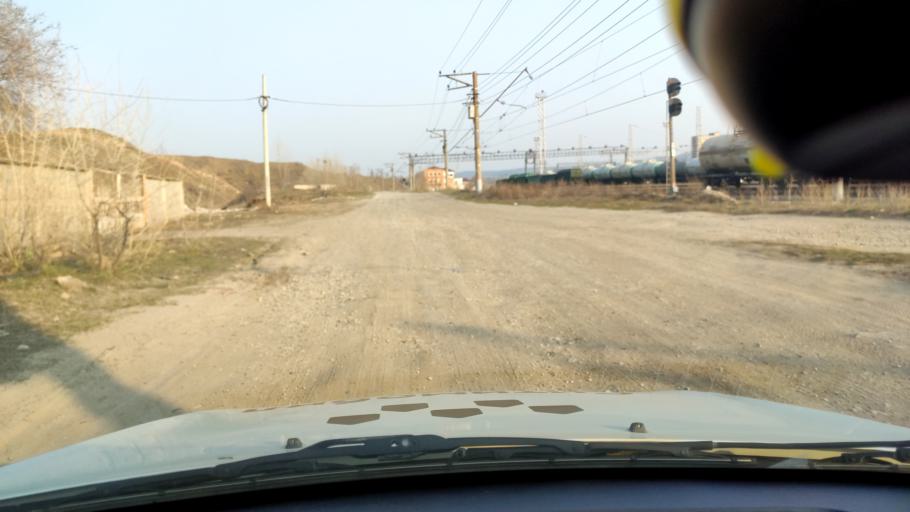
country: RU
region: Samara
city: Zhigulevsk
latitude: 53.4788
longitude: 49.5267
